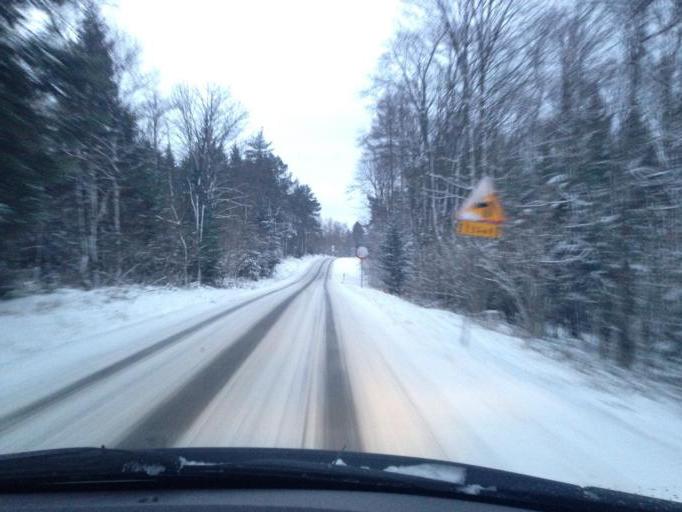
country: PL
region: Subcarpathian Voivodeship
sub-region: Powiat jasielski
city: Krempna
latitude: 49.5357
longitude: 21.4999
